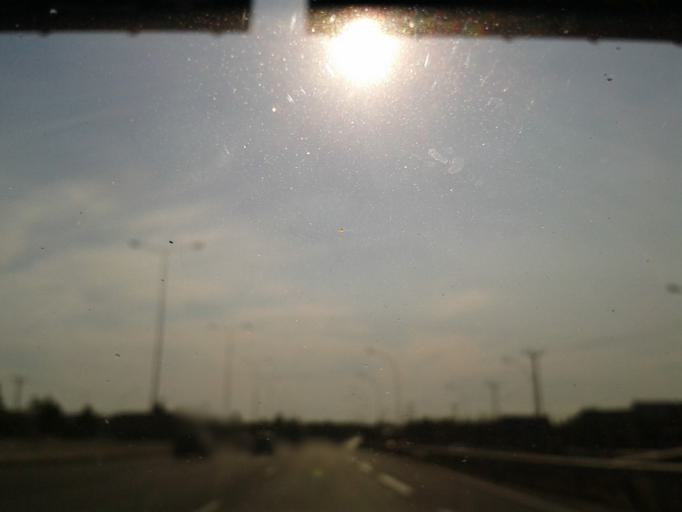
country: GR
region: Attica
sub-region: Nomarchia Athinas
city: Nea Erythraia
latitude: 38.1069
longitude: 23.8183
